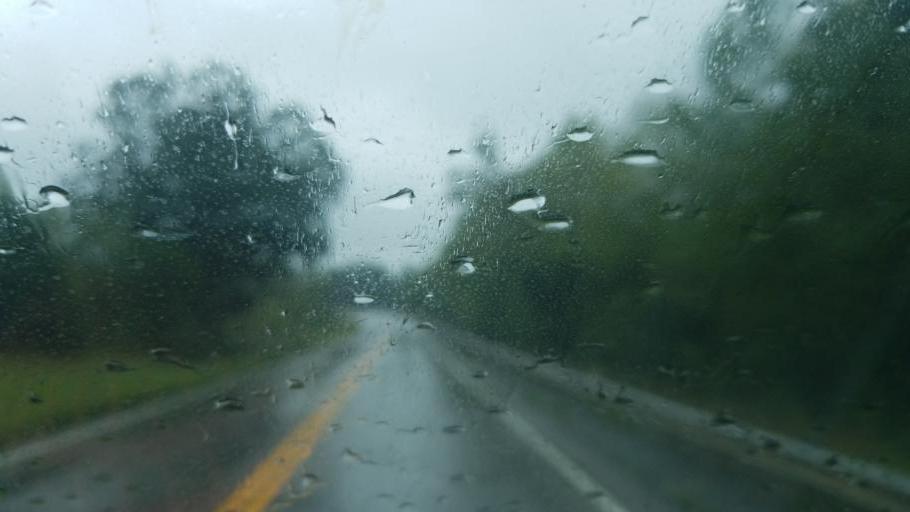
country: US
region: Kentucky
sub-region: Fleming County
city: Flemingsburg
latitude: 38.3292
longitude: -83.5899
